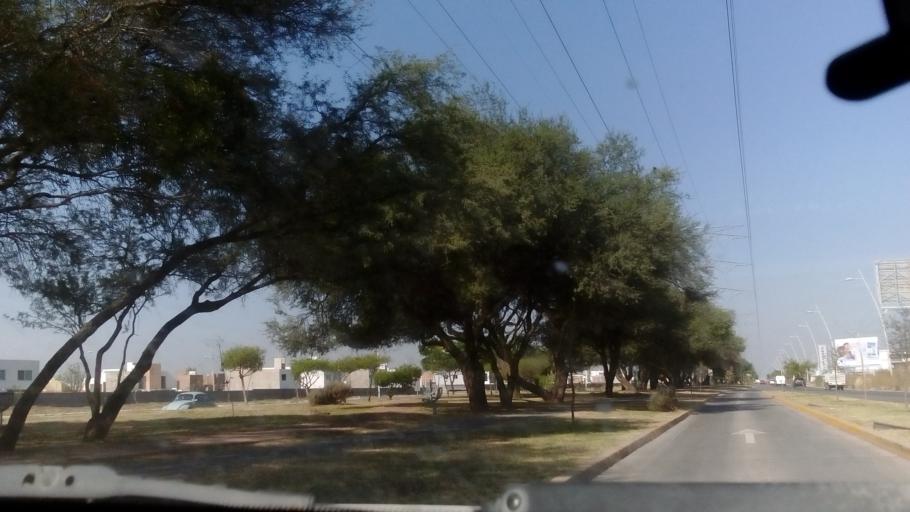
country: MX
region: Guanajuato
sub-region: Leon
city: Medina
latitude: 21.1320
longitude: -101.6089
